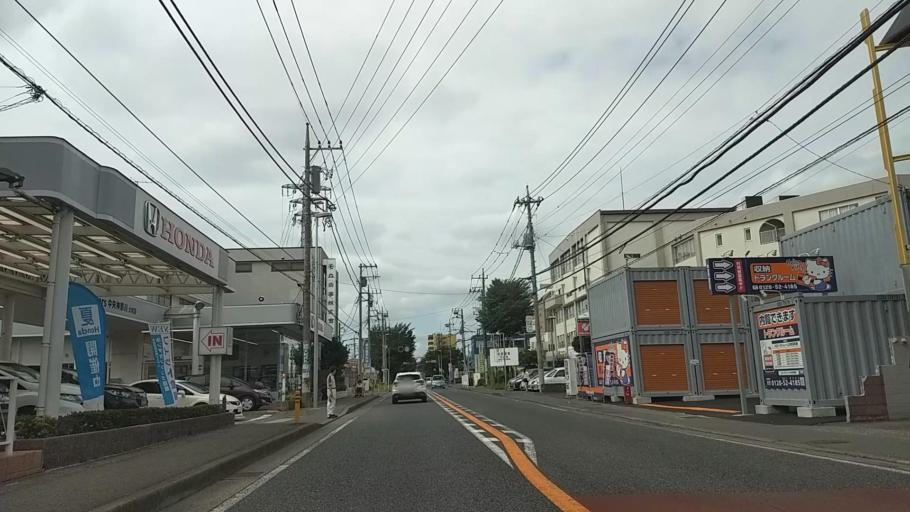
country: JP
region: Kanagawa
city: Minami-rinkan
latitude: 35.4758
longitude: 139.4650
